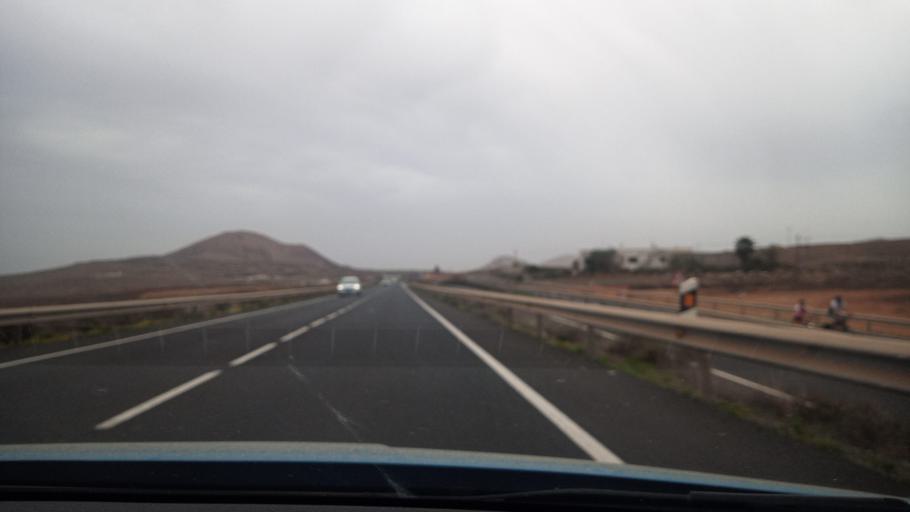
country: ES
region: Canary Islands
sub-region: Provincia de Las Palmas
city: Nazaret
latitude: 29.0314
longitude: -13.5223
